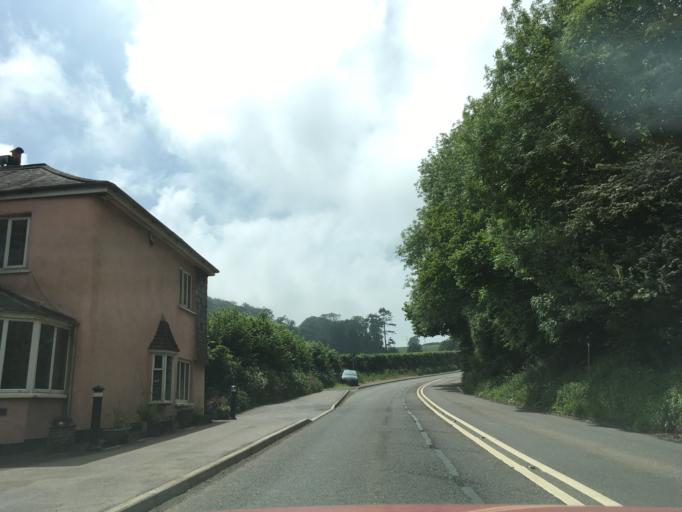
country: GB
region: England
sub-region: Devon
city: Totnes
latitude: 50.4252
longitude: -3.6912
